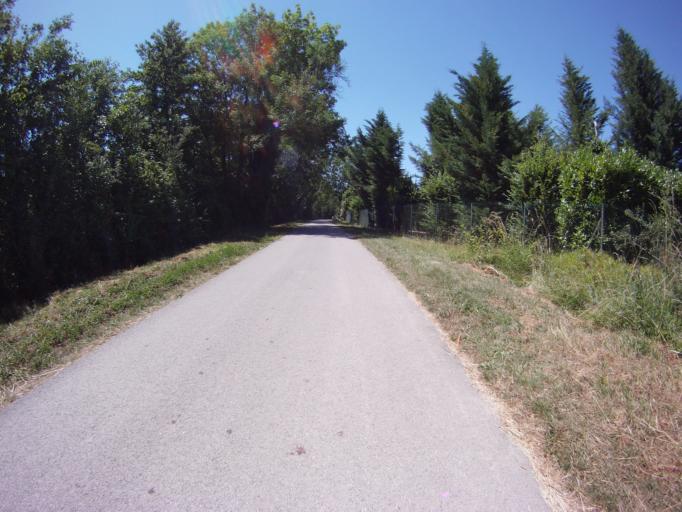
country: FR
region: Champagne-Ardenne
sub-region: Departement de la Marne
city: Damery
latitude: 49.0668
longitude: 3.8863
